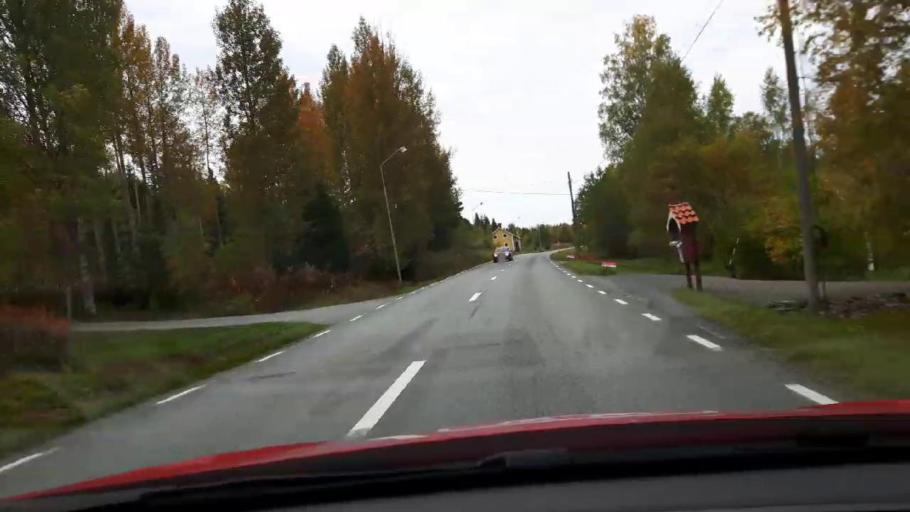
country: SE
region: Jaemtland
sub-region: Krokoms Kommun
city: Krokom
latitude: 63.1846
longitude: 14.0742
